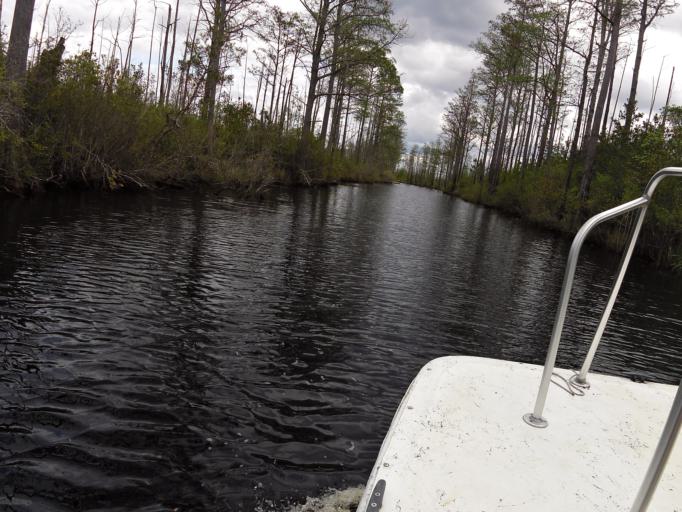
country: US
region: Georgia
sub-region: Charlton County
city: Folkston
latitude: 30.7354
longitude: -82.1590
